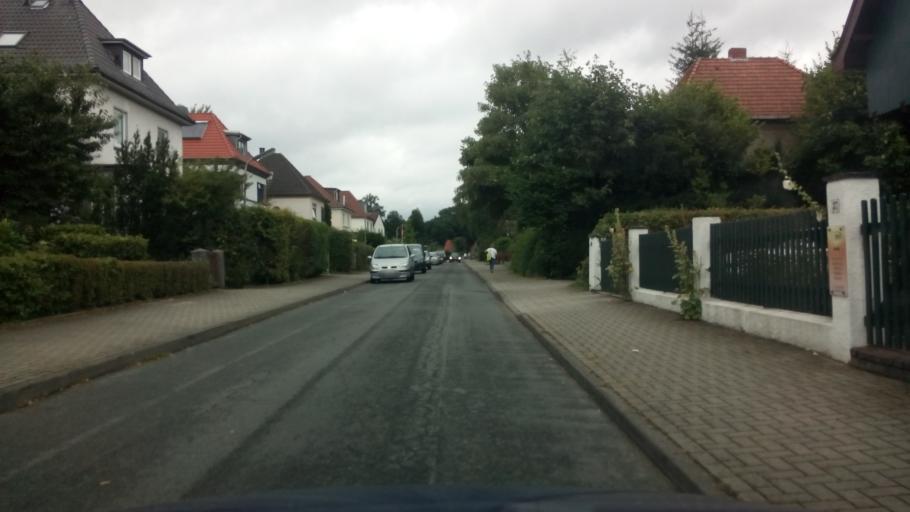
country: DE
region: Lower Saxony
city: Lemwerder
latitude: 53.1756
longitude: 8.6286
